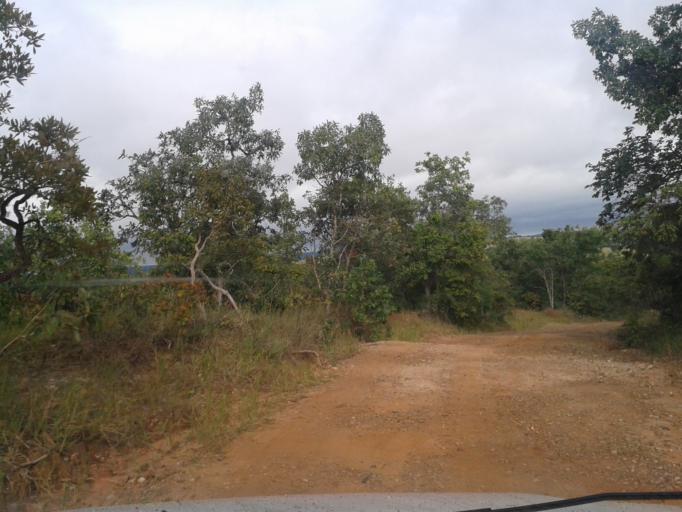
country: BR
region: Minas Gerais
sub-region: Campina Verde
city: Campina Verde
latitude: -19.4038
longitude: -49.6317
